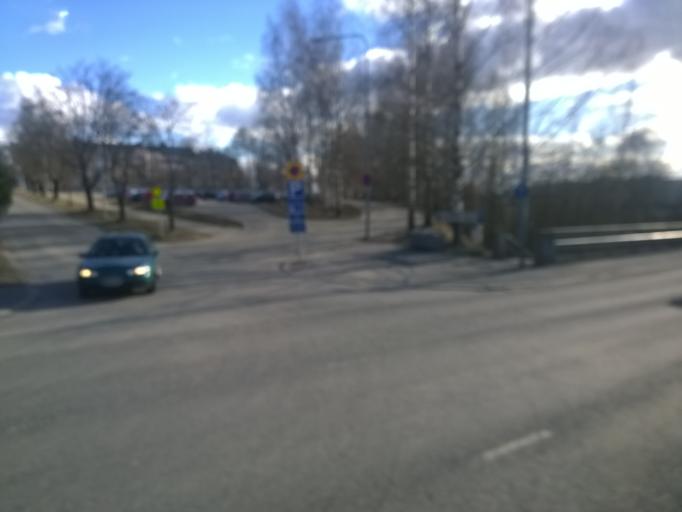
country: FI
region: Pirkanmaa
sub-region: Tampere
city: Tampere
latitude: 61.4953
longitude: 23.7837
